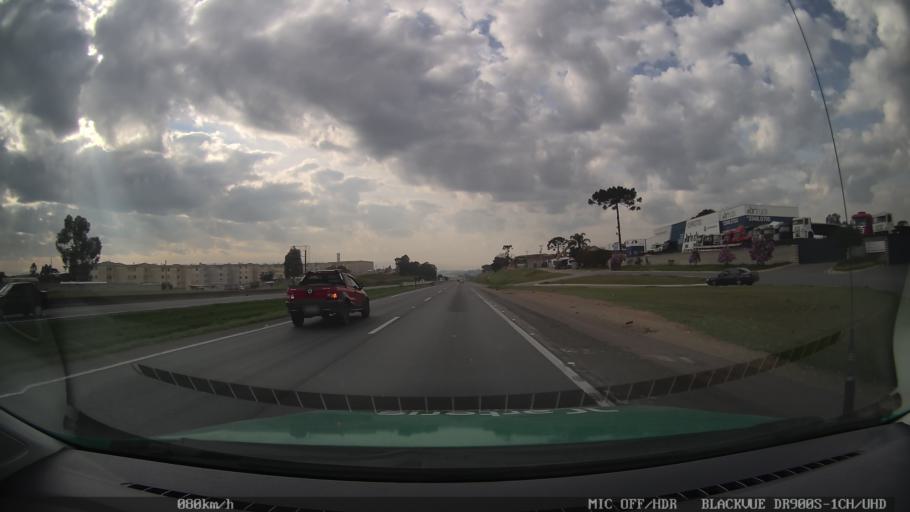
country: BR
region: Parana
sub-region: Sao Jose Dos Pinhais
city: Sao Jose dos Pinhais
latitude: -25.5638
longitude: -49.2550
